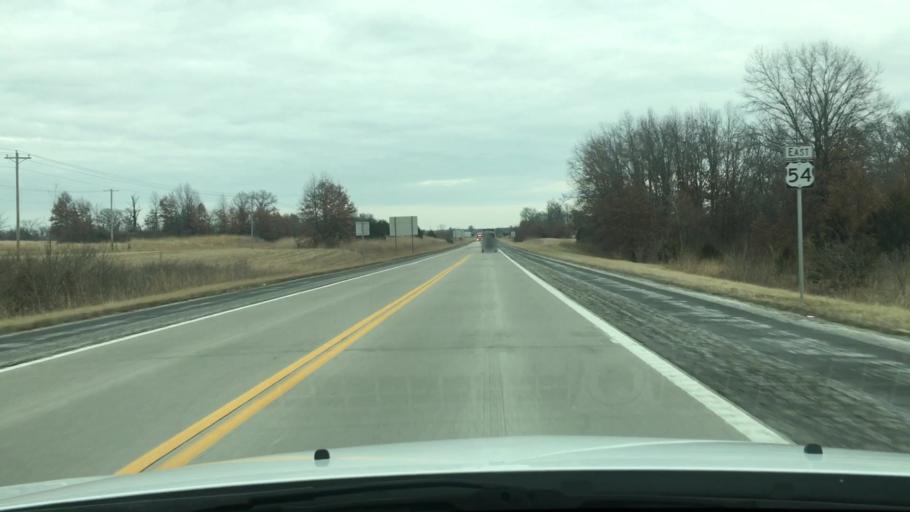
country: US
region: Missouri
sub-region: Audrain County
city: Mexico
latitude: 39.1220
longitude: -91.8789
